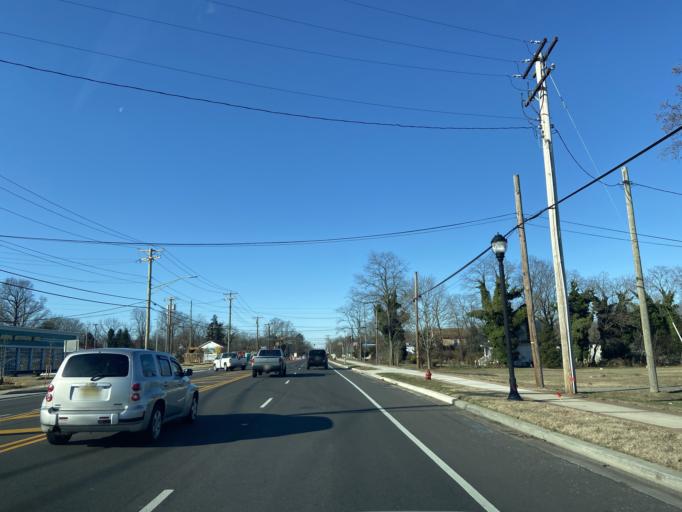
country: US
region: New Jersey
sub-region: Cumberland County
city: Vineland
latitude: 39.4875
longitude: -75.0503
